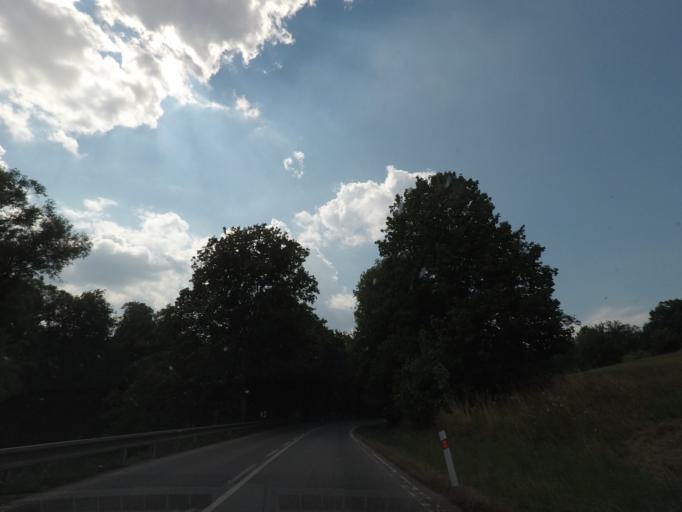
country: CZ
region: Kralovehradecky
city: Pilnikov
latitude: 50.5504
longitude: 15.8436
